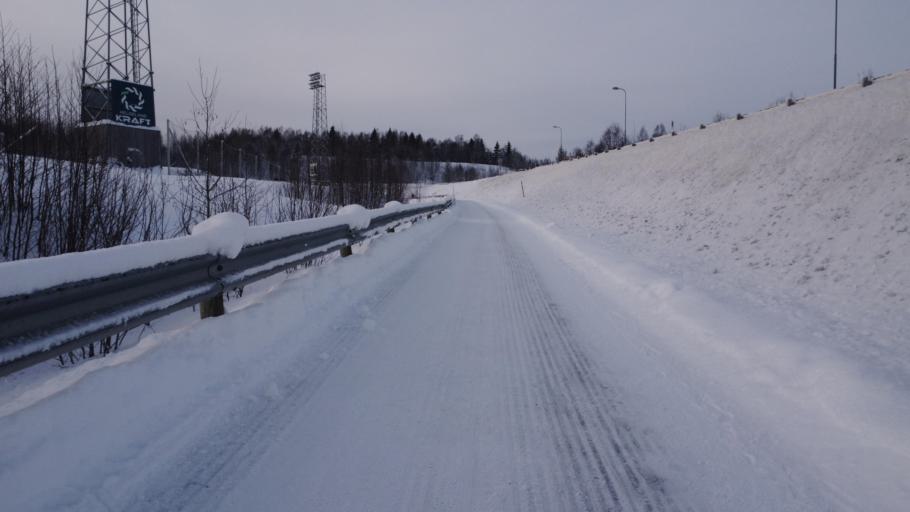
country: NO
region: Nordland
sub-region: Rana
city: Mo i Rana
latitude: 66.3238
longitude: 14.1620
